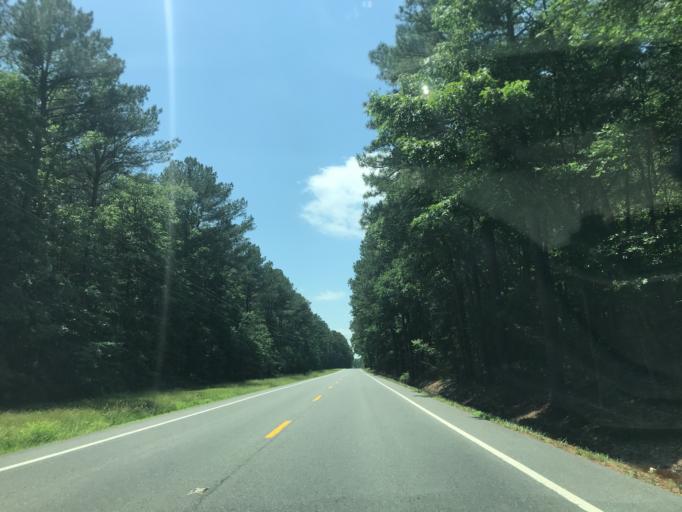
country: US
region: Maryland
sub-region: Dorchester County
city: Hurlock
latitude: 38.6334
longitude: -75.7926
